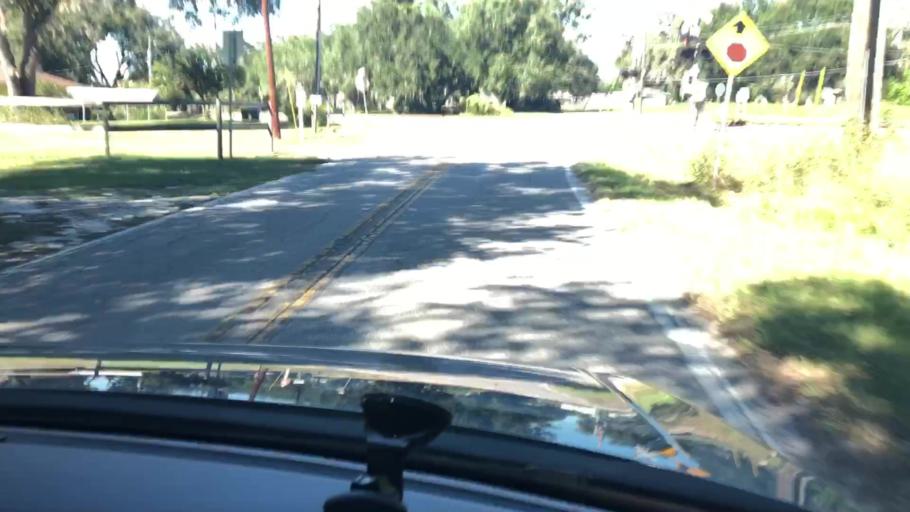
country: US
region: Florida
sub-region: Polk County
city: Kathleen
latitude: 28.1196
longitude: -82.0251
